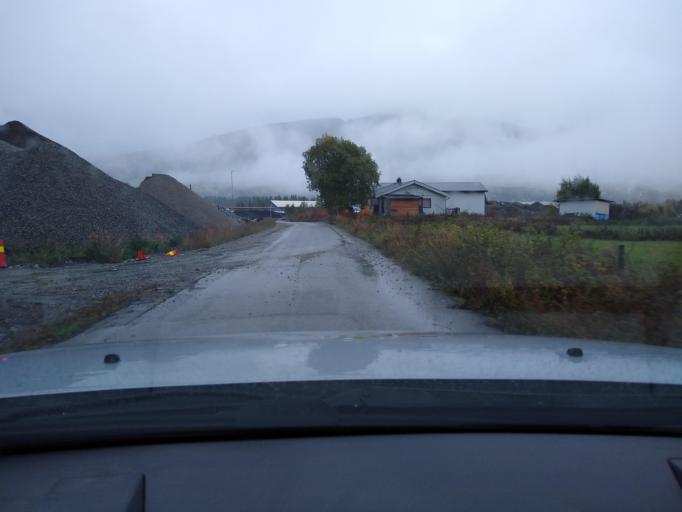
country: NO
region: Oppland
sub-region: Ringebu
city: Ringebu
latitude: 61.5422
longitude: 10.0541
